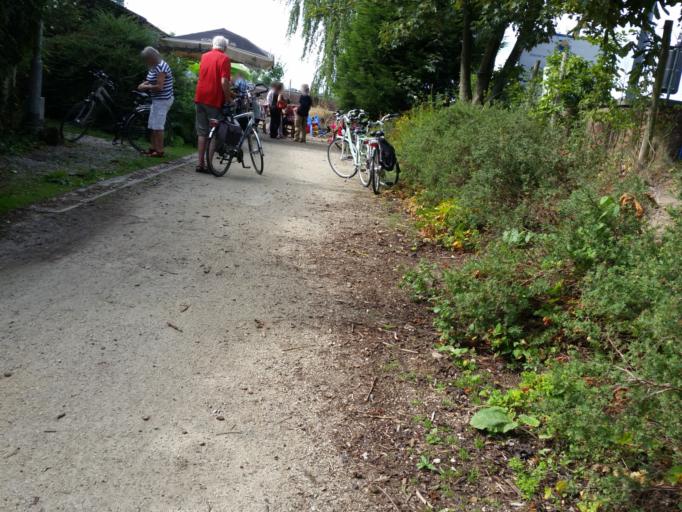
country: BE
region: Flanders
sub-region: Provincie Antwerpen
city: Rumst
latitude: 51.0637
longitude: 4.4303
